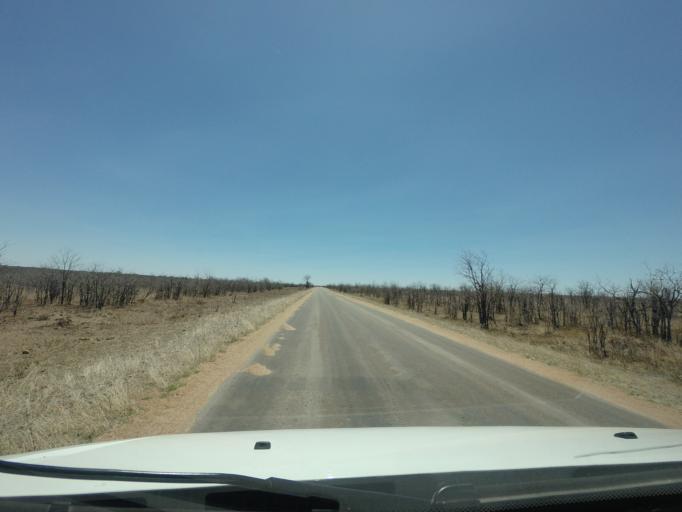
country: ZA
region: Limpopo
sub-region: Mopani District Municipality
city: Phalaborwa
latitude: -23.5760
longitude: 31.4511
